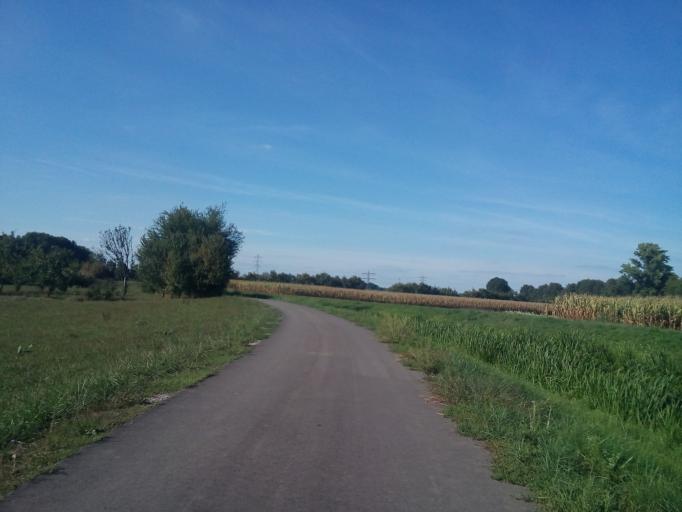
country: DE
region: Baden-Wuerttemberg
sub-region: Karlsruhe Region
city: Zell
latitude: 48.6681
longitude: 8.0726
